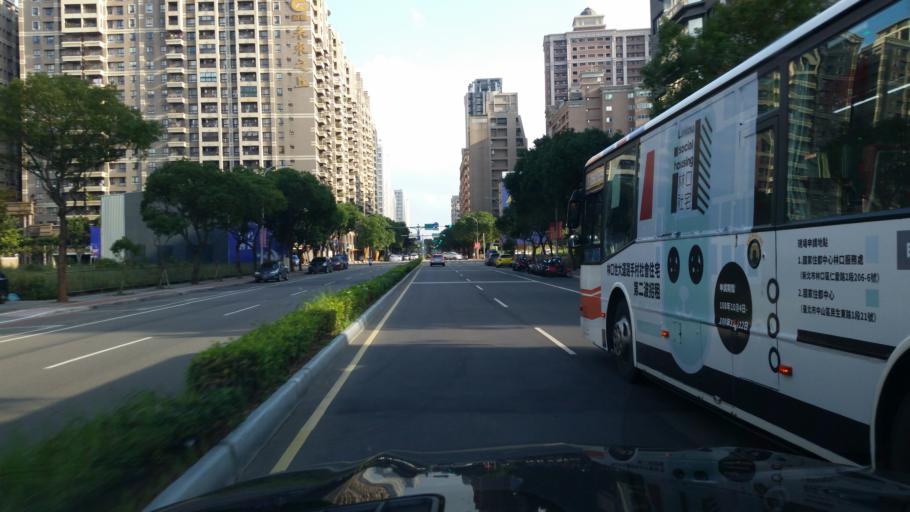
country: TW
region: Taiwan
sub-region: Taoyuan
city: Taoyuan
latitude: 25.0790
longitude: 121.3716
